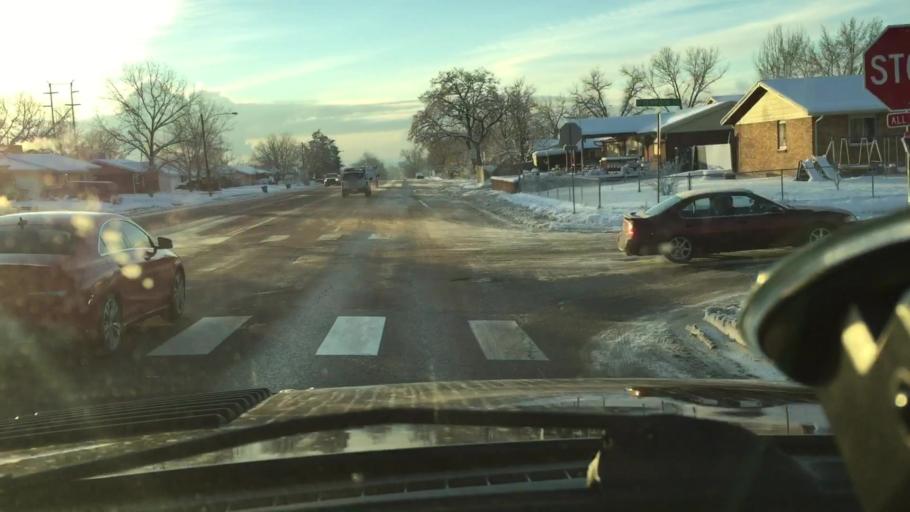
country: US
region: Colorado
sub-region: Adams County
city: Sherrelwood
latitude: 39.8395
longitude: -105.0009
